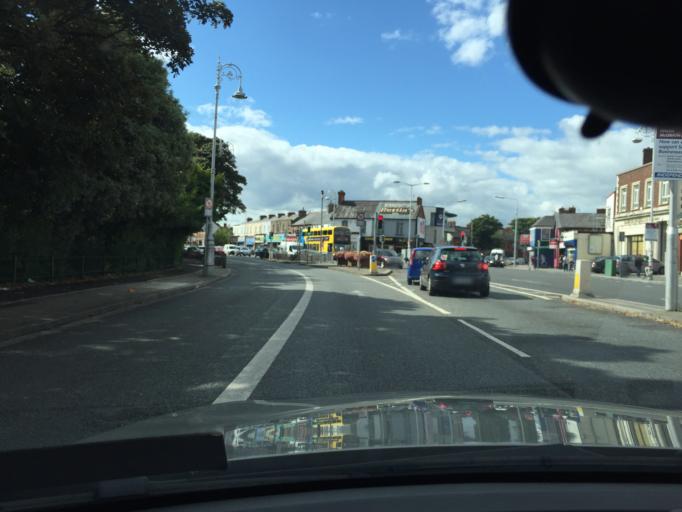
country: IE
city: Fairview
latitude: 53.3630
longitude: -6.2357
